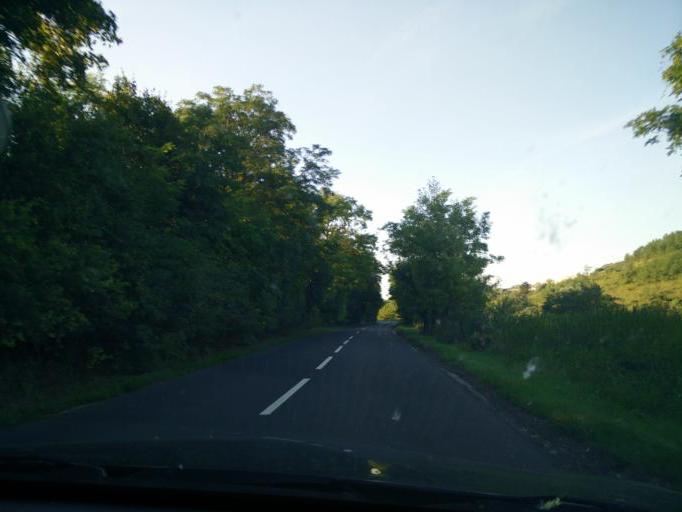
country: HU
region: Pest
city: Piliscsaba
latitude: 47.6436
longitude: 18.7831
